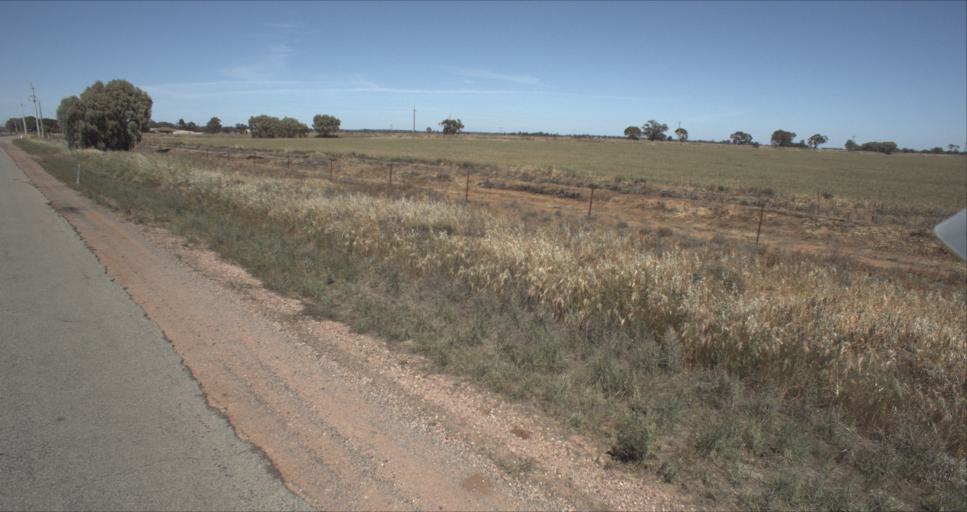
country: AU
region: New South Wales
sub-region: Leeton
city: Leeton
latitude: -34.5653
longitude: 146.3119
